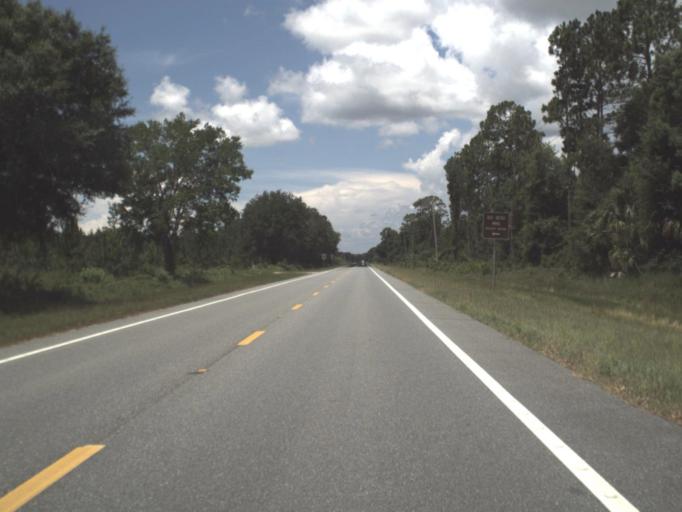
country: US
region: Florida
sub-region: Taylor County
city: Perry
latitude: 30.1429
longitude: -83.8367
